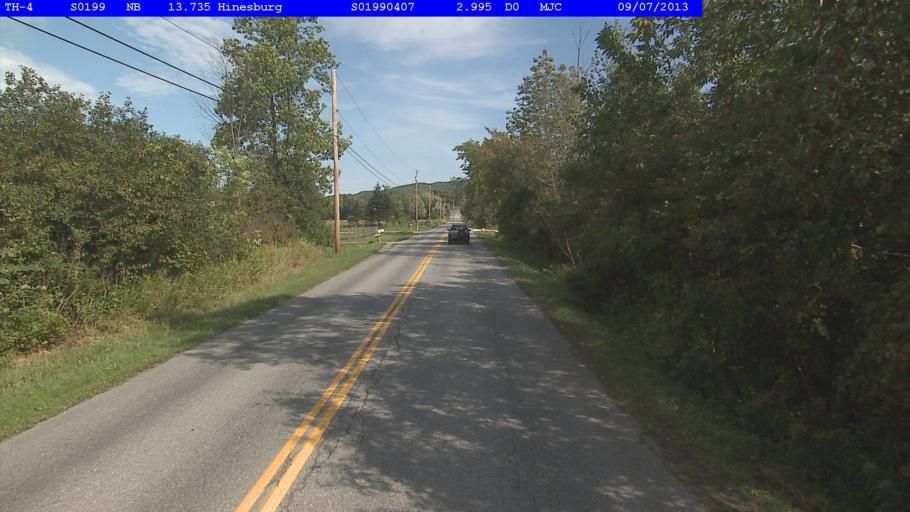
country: US
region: Vermont
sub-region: Chittenden County
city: Hinesburg
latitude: 44.3210
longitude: -73.1100
